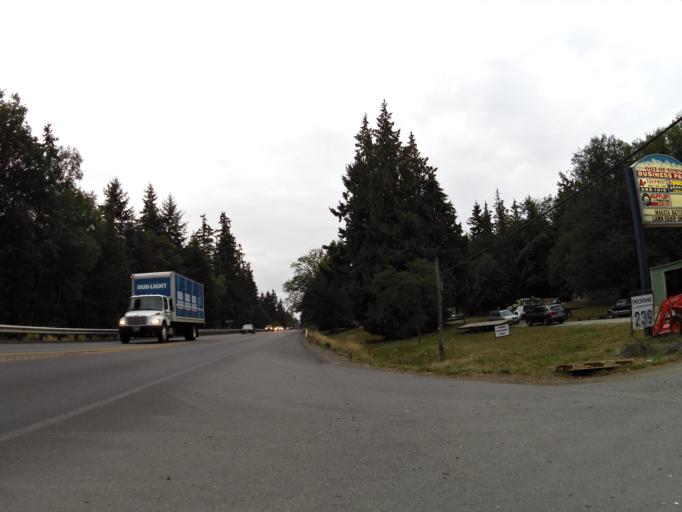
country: US
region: Washington
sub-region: Jefferson County
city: Port Townsend
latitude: 48.0961
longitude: -122.8154
